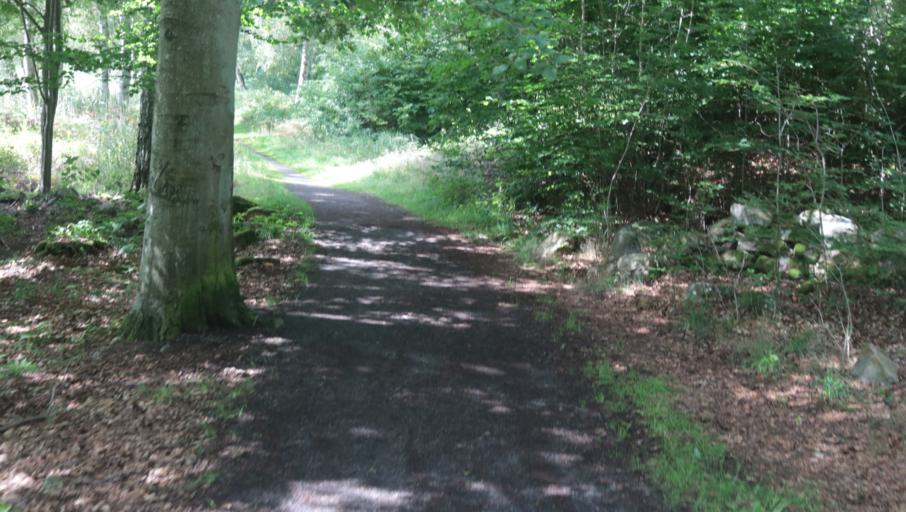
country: SE
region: Blekinge
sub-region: Karlshamns Kommun
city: Karlshamn
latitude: 56.1855
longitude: 14.8713
